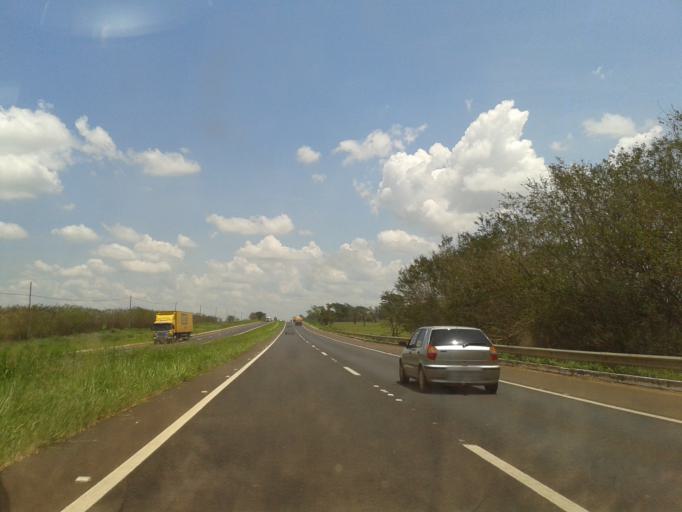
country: BR
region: Minas Gerais
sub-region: Uberlandia
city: Uberlandia
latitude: -18.8785
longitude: -48.5071
